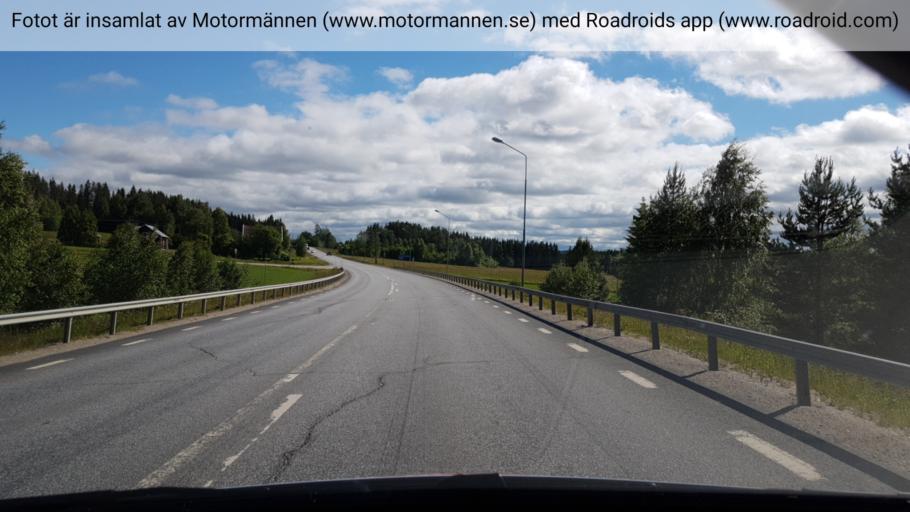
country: SE
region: Vaesterbotten
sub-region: Vannas Kommun
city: Vaennaes
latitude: 63.9846
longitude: 19.7291
